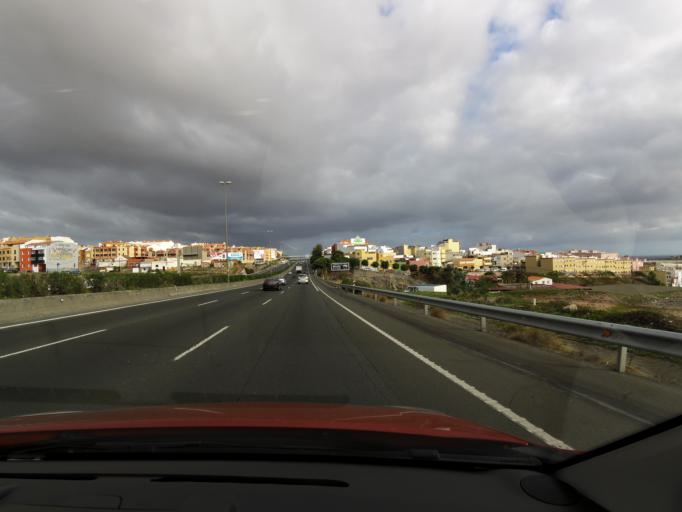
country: ES
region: Canary Islands
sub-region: Provincia de Las Palmas
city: Telde
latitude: 27.9886
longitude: -15.3922
